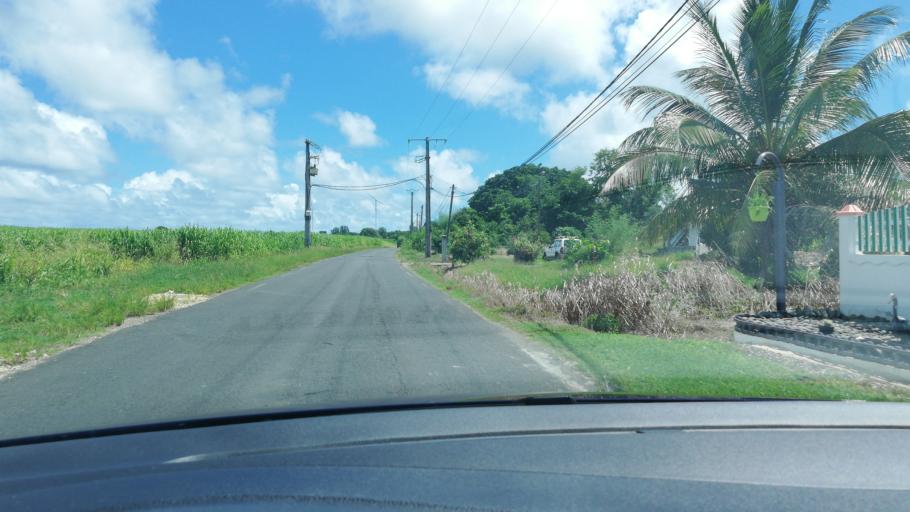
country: GP
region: Guadeloupe
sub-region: Guadeloupe
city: Petit-Canal
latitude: 16.3800
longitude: -61.4367
